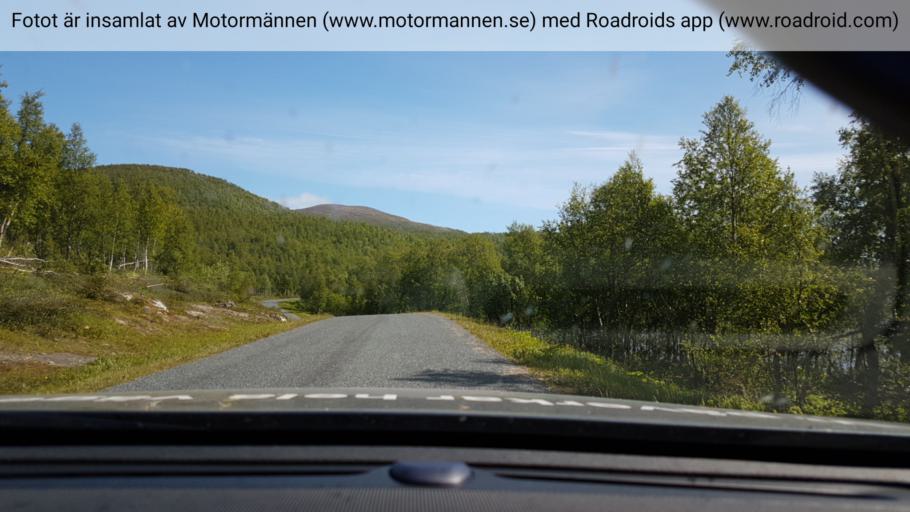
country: NO
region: Nordland
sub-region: Hattfjelldal
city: Hattfjelldal
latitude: 65.4167
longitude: 14.6963
